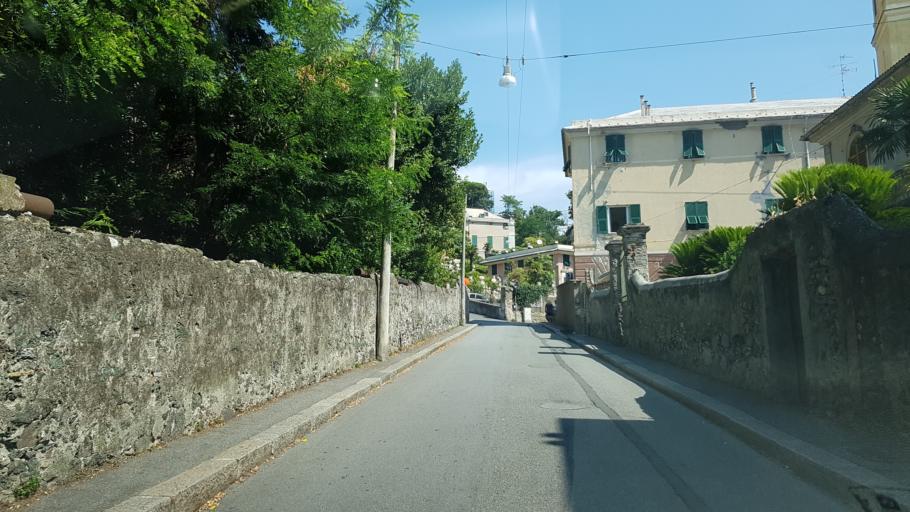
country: IT
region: Liguria
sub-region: Provincia di Genova
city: San Teodoro
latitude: 44.4166
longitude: 8.8693
